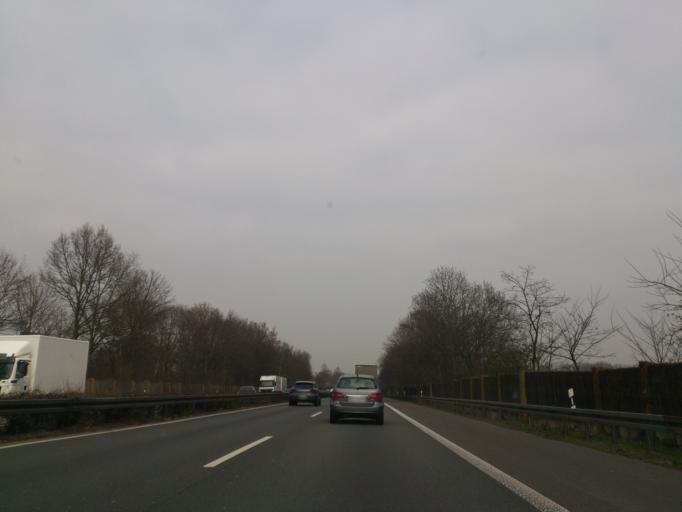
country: DE
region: North Rhine-Westphalia
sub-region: Regierungsbezirk Dusseldorf
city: Monchengladbach
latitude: 51.2378
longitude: 6.4651
